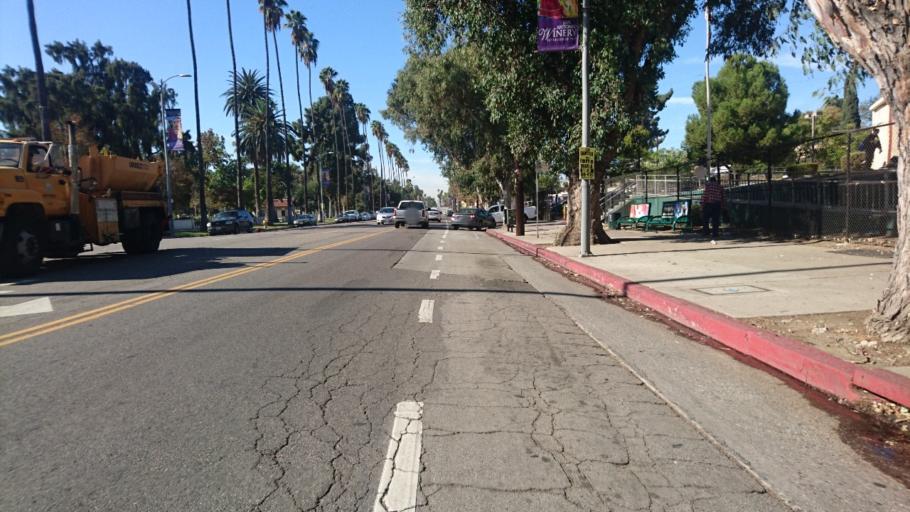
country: US
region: California
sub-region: Los Angeles County
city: Boyle Heights
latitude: 34.0678
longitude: -118.2026
